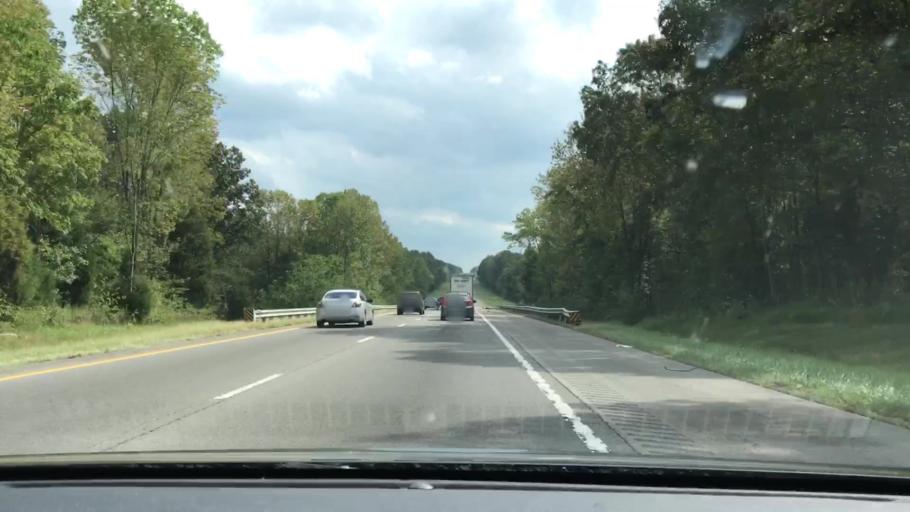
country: US
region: Tennessee
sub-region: Cheatham County
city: Pleasant View
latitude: 36.4599
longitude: -87.1148
